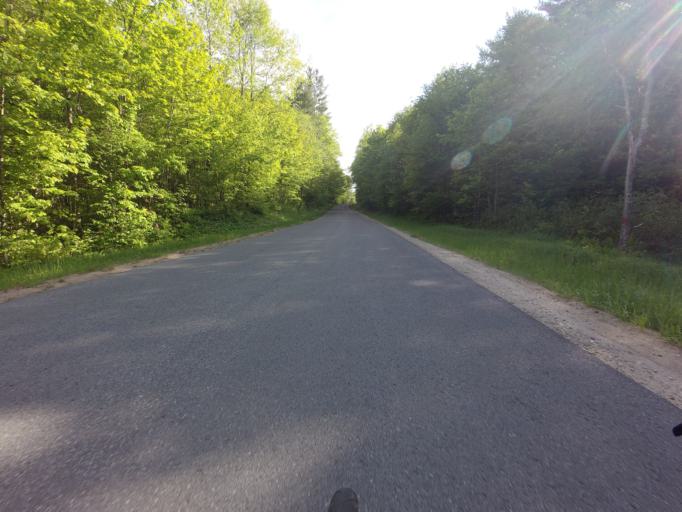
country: US
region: New York
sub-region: St. Lawrence County
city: Gouverneur
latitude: 44.2087
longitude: -75.2496
